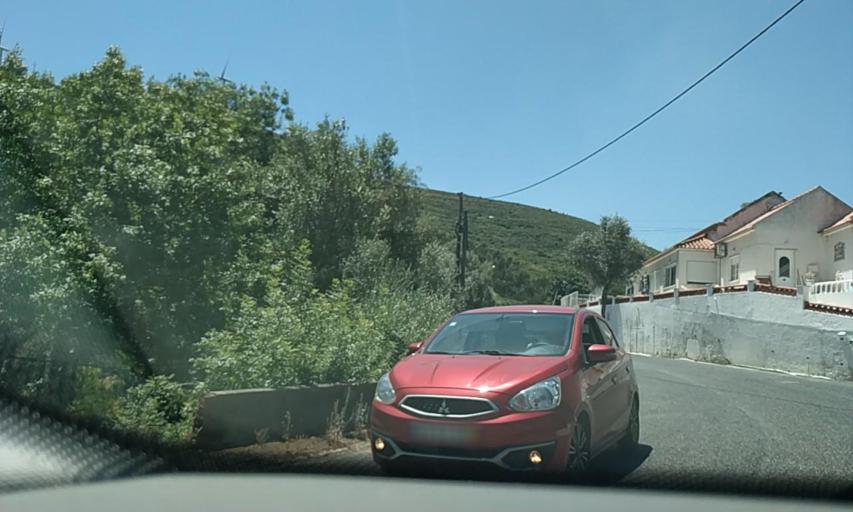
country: PT
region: Lisbon
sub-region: Sintra
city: Almargem
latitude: 38.8675
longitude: -9.2240
